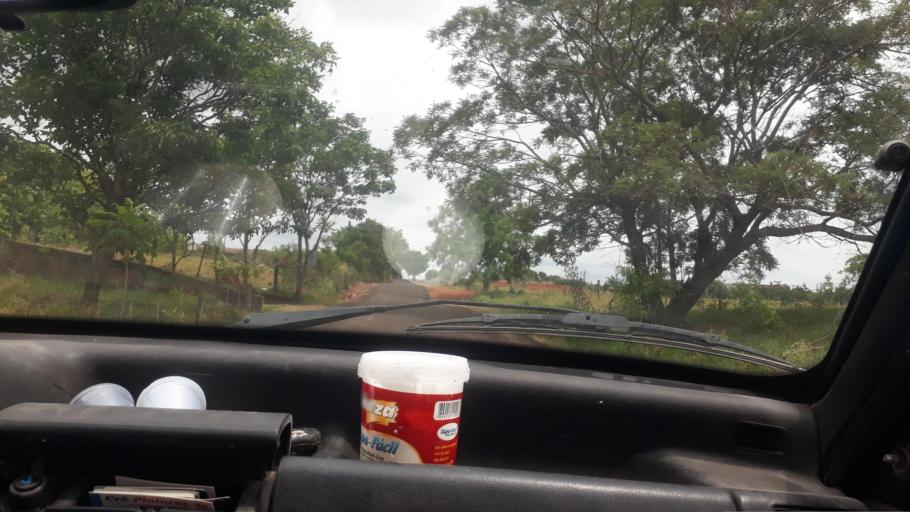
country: BR
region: Sao Paulo
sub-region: Regente Feijo
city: Regente Feijo
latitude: -22.2341
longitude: -51.3000
